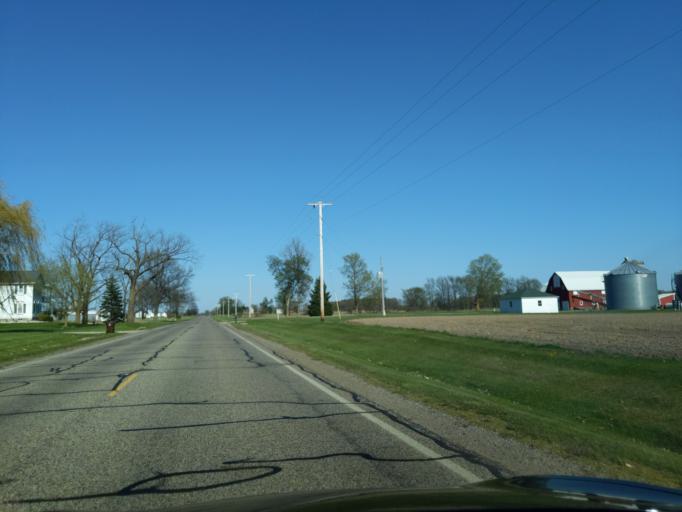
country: US
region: Michigan
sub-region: Ionia County
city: Ionia
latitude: 42.8858
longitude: -85.0181
